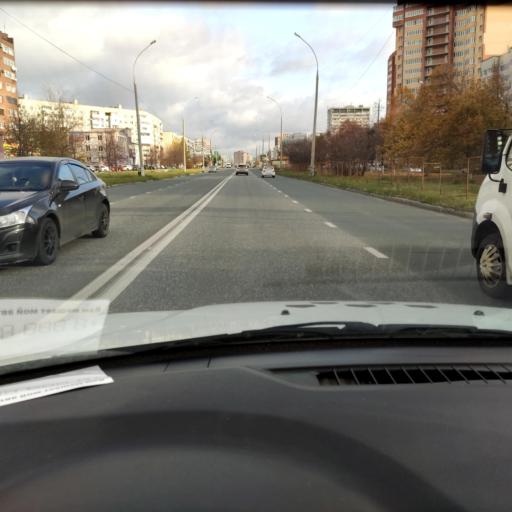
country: RU
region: Samara
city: Tol'yatti
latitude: 53.5417
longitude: 49.3392
